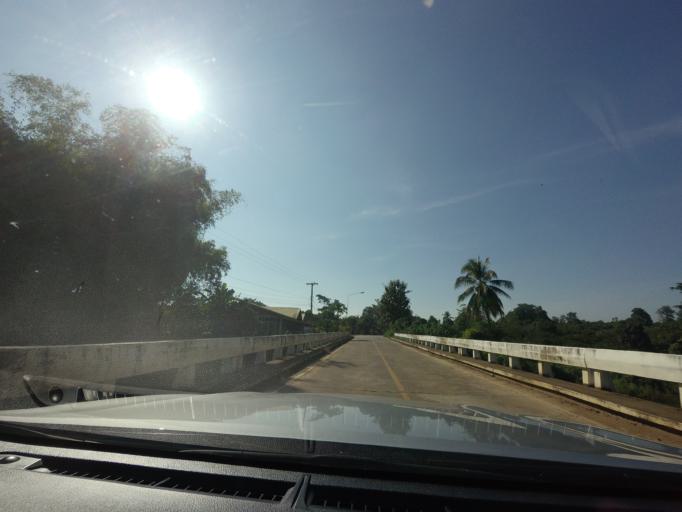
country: TH
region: Sukhothai
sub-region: Amphoe Si Satchanalai
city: Si Satchanalai
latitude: 17.6966
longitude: 99.7013
